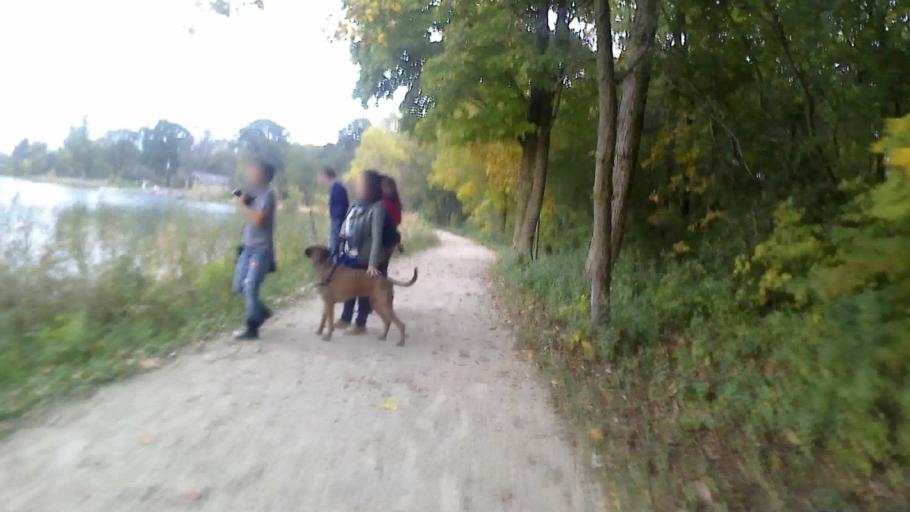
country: US
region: Illinois
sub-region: DuPage County
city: Warrenville
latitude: 41.8258
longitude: -88.1419
